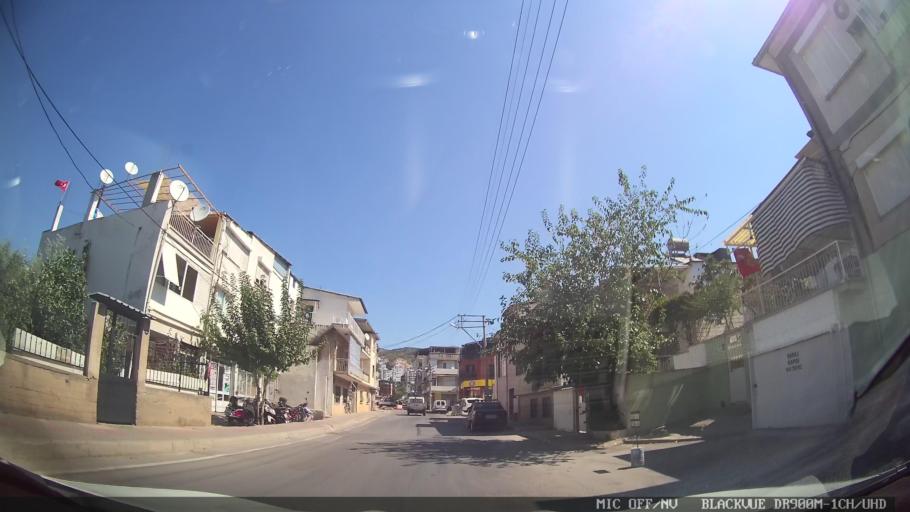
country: TR
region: Izmir
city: Karsiyaka
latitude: 38.4958
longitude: 27.0668
